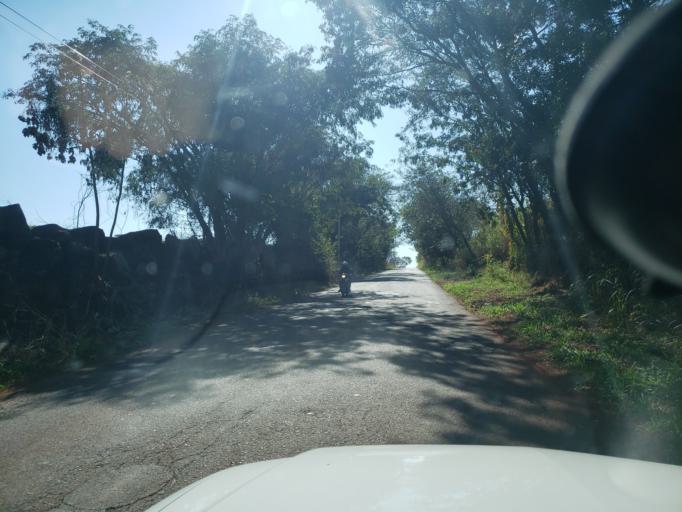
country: BR
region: Sao Paulo
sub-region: Moji-Guacu
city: Mogi-Gaucu
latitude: -22.3428
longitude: -46.8898
